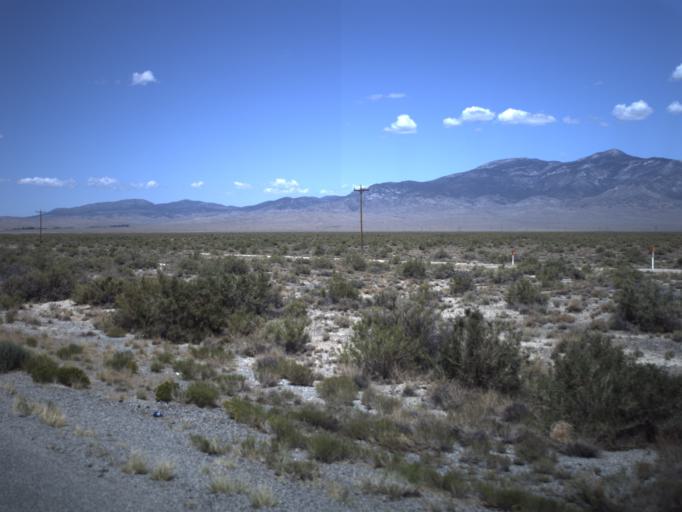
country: US
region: Nevada
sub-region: White Pine County
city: McGill
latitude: 39.0564
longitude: -114.0394
